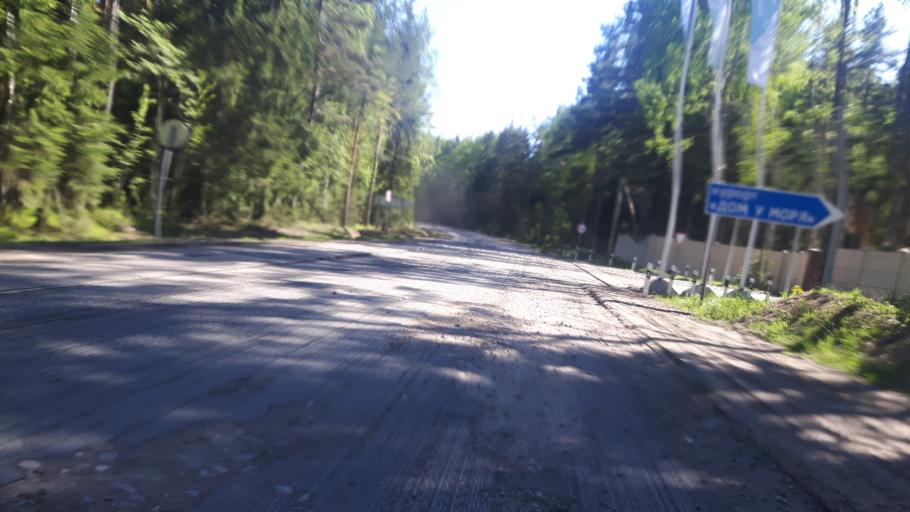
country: RU
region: Leningrad
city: Sosnovyy Bor
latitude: 60.2301
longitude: 29.0021
